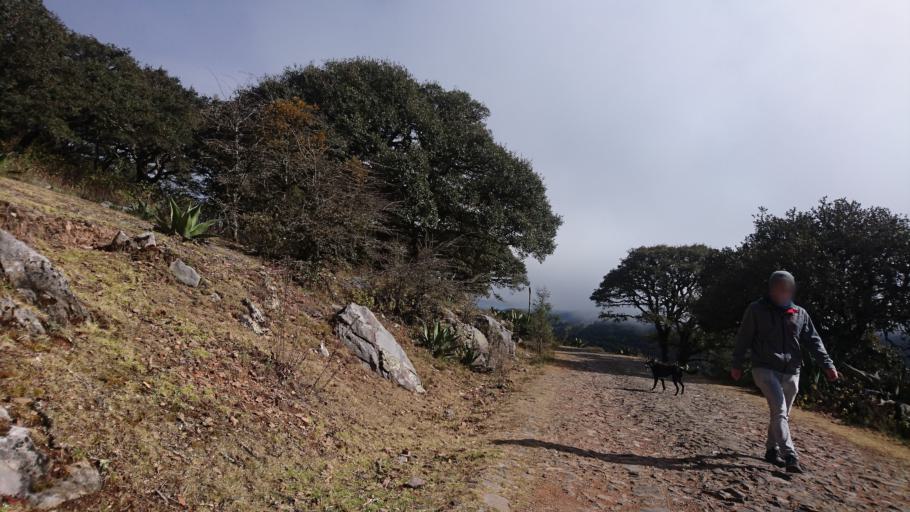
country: MX
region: San Luis Potosi
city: Zaragoza
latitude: 22.0659
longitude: -100.6432
